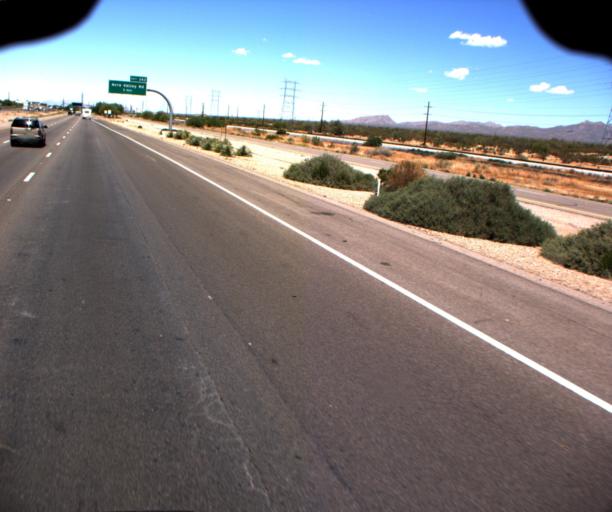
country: US
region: Arizona
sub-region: Pima County
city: Tortolita
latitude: 32.3865
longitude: -111.1154
